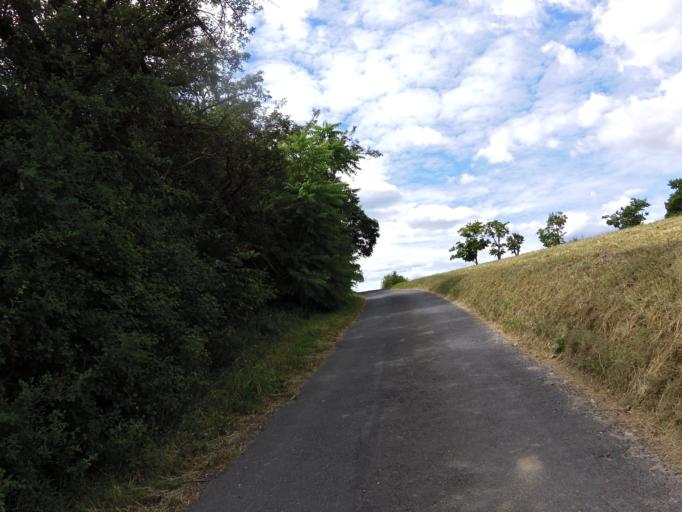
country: DE
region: Bavaria
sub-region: Regierungsbezirk Unterfranken
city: Veitshochheim
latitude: 49.8147
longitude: 9.8991
